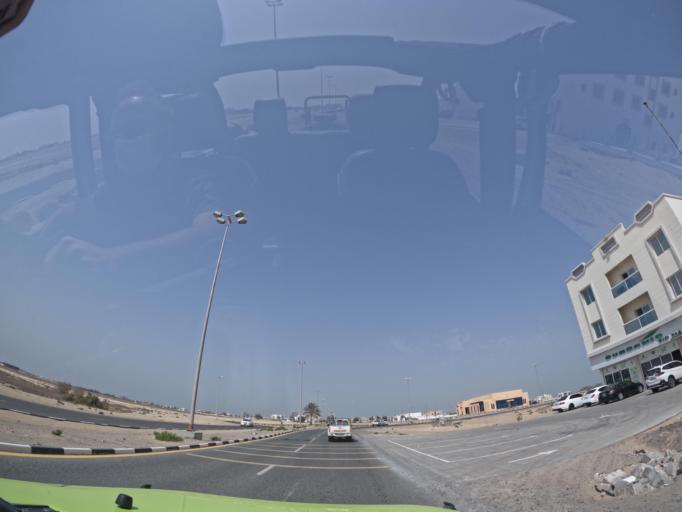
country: AE
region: Umm al Qaywayn
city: Umm al Qaywayn
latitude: 25.5207
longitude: 55.5542
